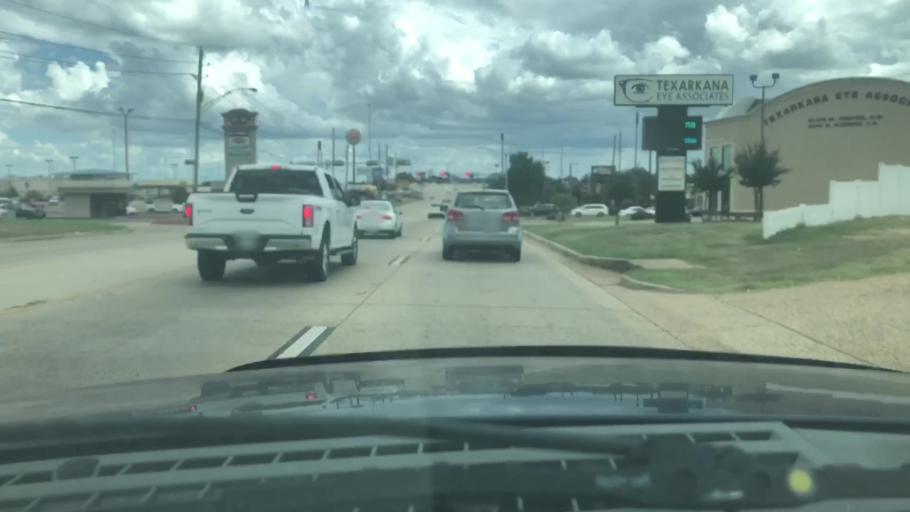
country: US
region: Texas
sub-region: Bowie County
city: Wake Village
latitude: 33.4602
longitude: -94.0906
